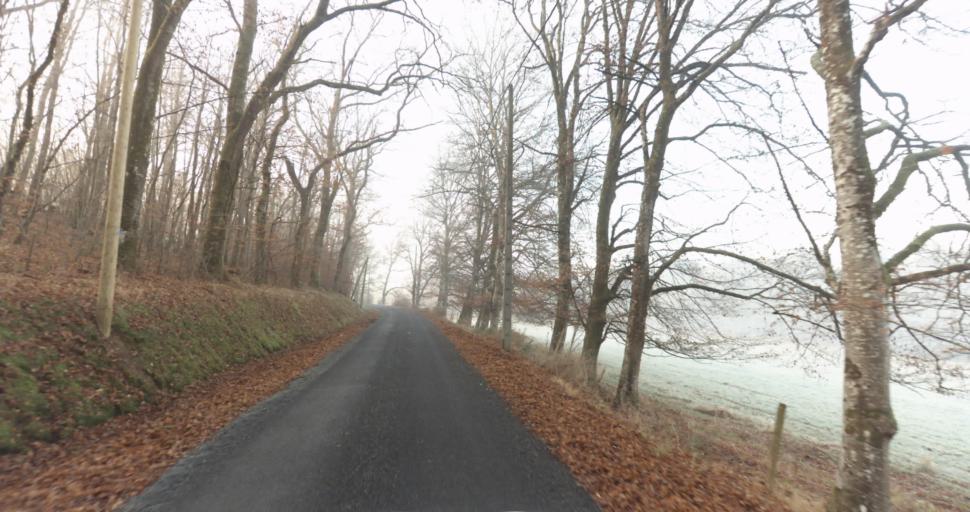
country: FR
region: Limousin
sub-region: Departement de la Haute-Vienne
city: Saint-Priest-sous-Aixe
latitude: 45.8132
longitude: 1.1181
